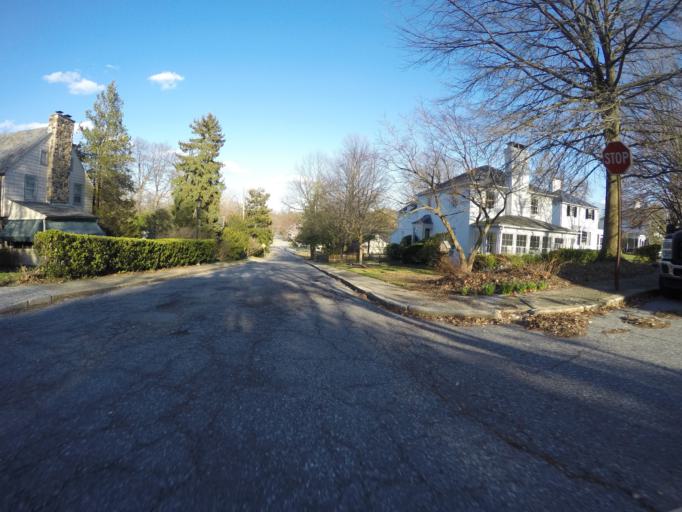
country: US
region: Maryland
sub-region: Baltimore County
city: Towson
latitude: 39.3545
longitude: -76.6179
